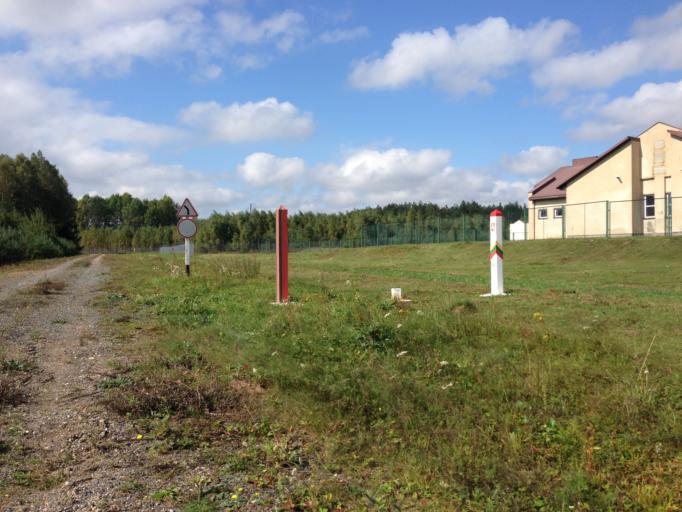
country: LT
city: Salcininkai
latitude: 54.2728
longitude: 25.3762
